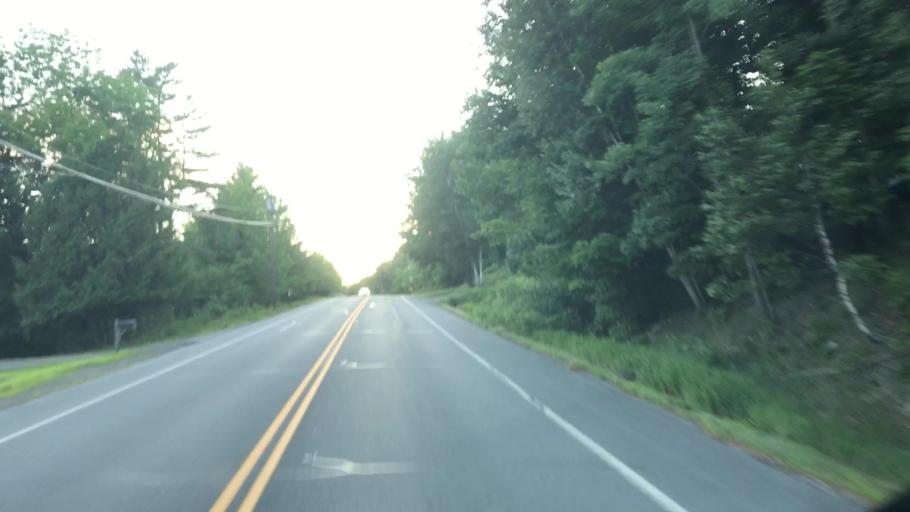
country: US
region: Maine
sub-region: Penobscot County
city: Lincoln
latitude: 45.3739
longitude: -68.4744
